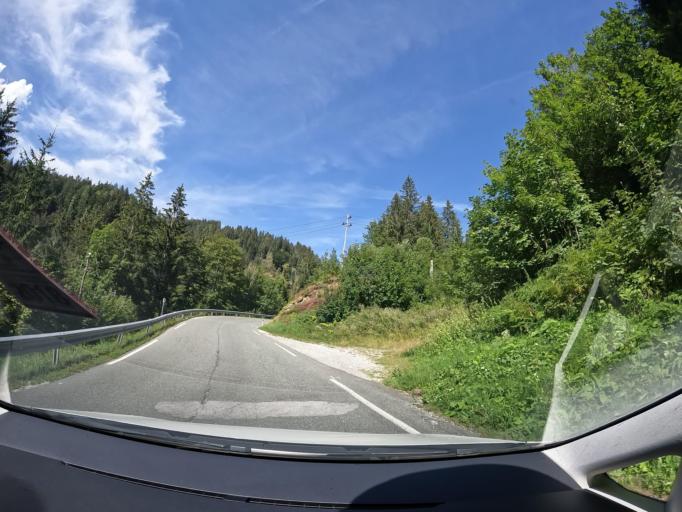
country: AT
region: Carinthia
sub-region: Politischer Bezirk Villach Land
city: Sankt Jakob
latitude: 46.5516
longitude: 14.0796
